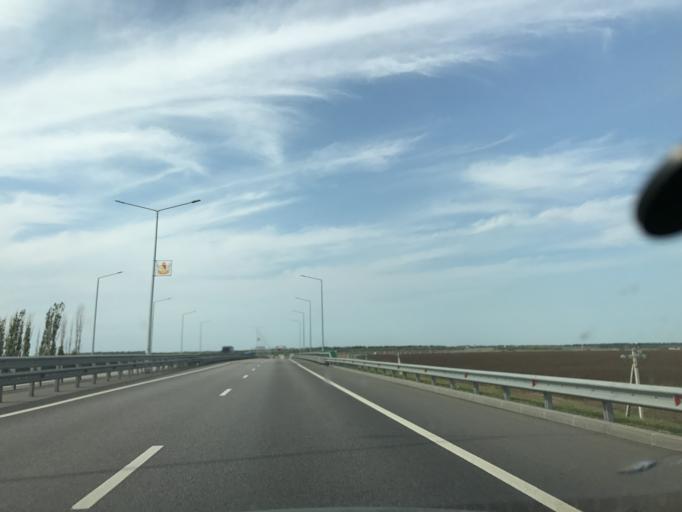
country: RU
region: Voronezj
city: Kashirskoye
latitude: 51.4816
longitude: 39.5461
